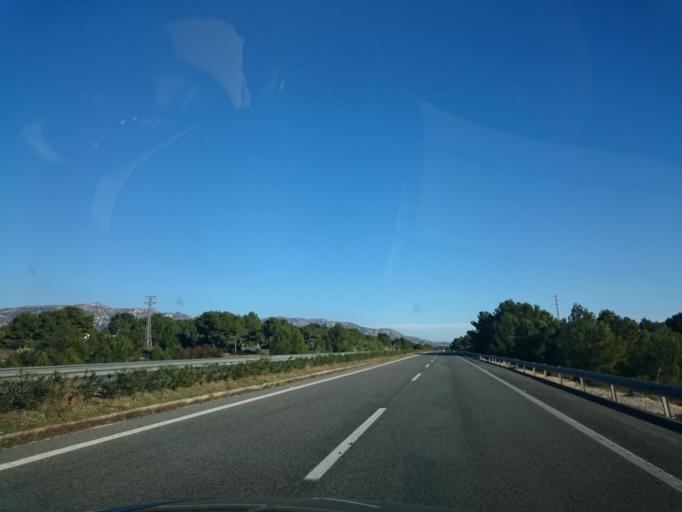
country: ES
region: Catalonia
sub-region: Provincia de Tarragona
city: l'Ametlla de Mar
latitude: 40.9015
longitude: 0.8140
